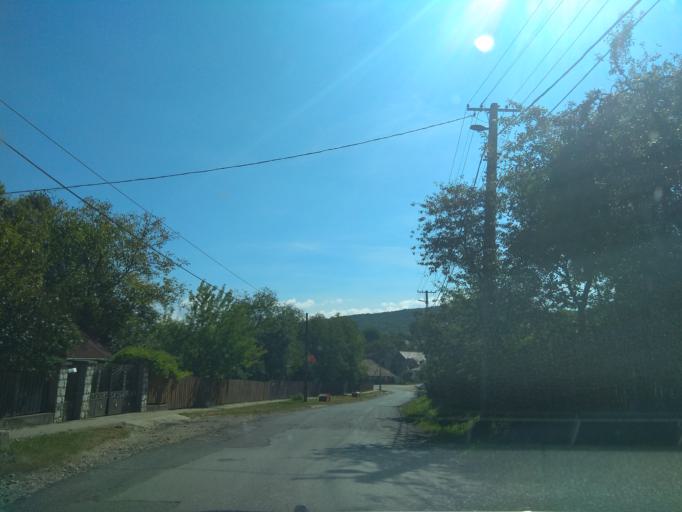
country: HU
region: Borsod-Abauj-Zemplen
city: Sajokaza
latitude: 48.1703
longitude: 20.5281
